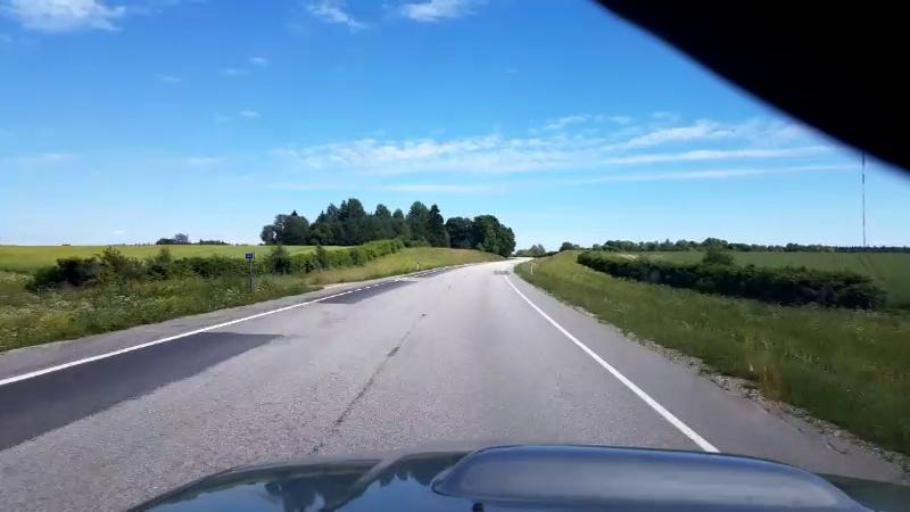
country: EE
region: Jaervamaa
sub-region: Koeru vald
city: Koeru
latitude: 58.9855
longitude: 26.0240
